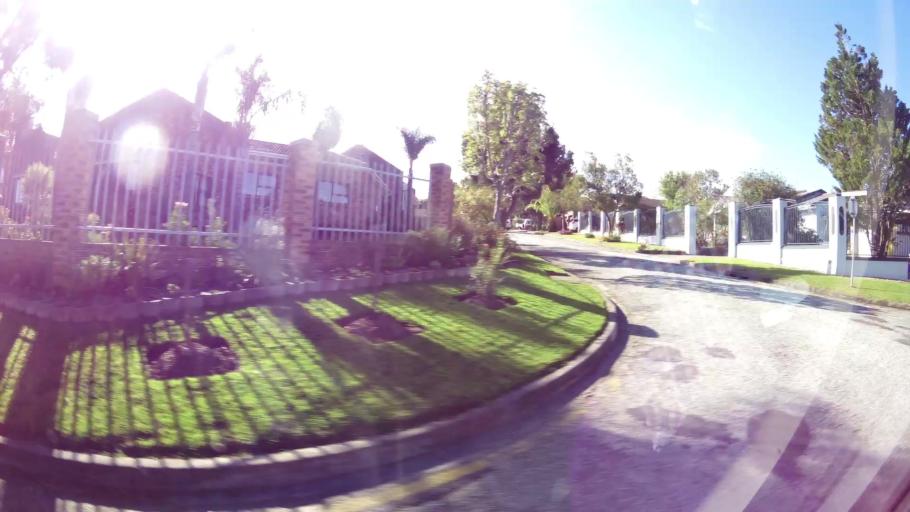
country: ZA
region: Western Cape
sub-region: Eden District Municipality
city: George
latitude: -33.9679
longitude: 22.4953
